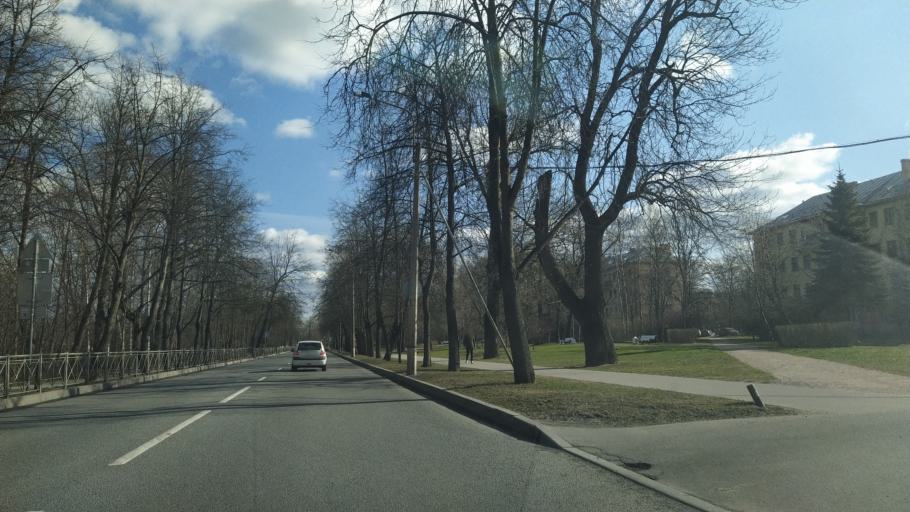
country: RU
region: St.-Petersburg
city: Pushkin
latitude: 59.7062
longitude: 30.4170
